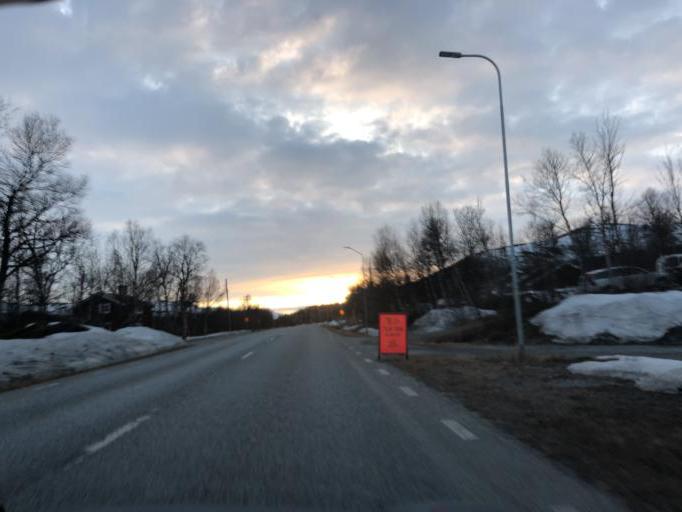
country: NO
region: Sor-Trondelag
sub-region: Tydal
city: Aas
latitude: 62.5491
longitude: 12.3090
